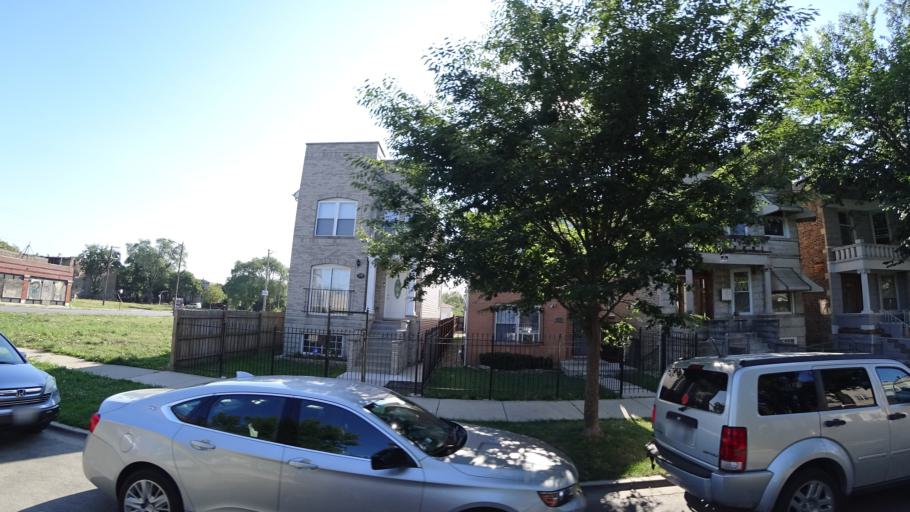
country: US
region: Illinois
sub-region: Cook County
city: Cicero
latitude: 41.8588
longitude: -87.7128
